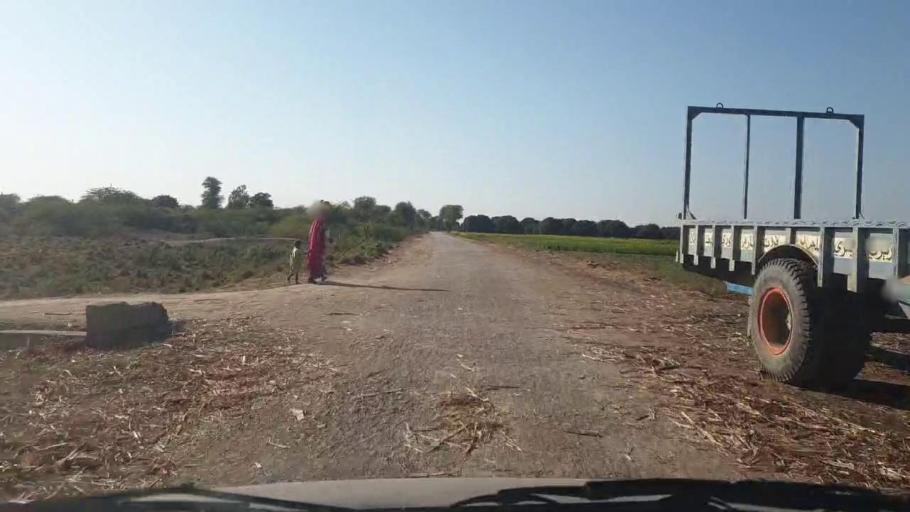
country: PK
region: Sindh
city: Samaro
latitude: 25.3515
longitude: 69.3117
